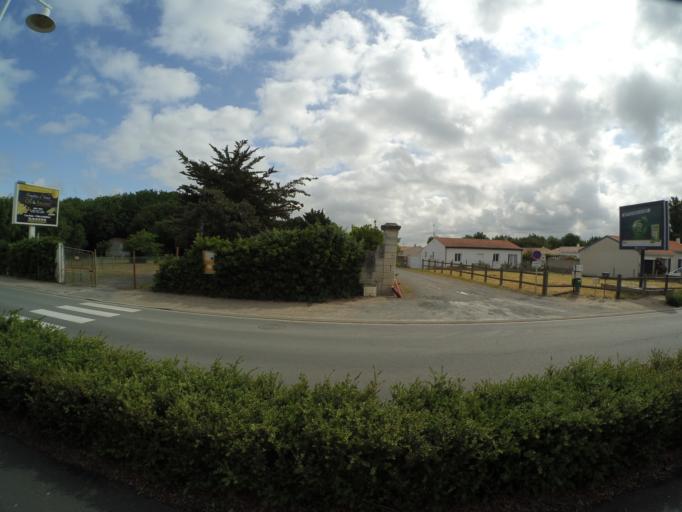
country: FR
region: Poitou-Charentes
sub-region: Departement de la Charente-Maritime
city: Chatelaillon-Plage
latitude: 46.0874
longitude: -1.0959
